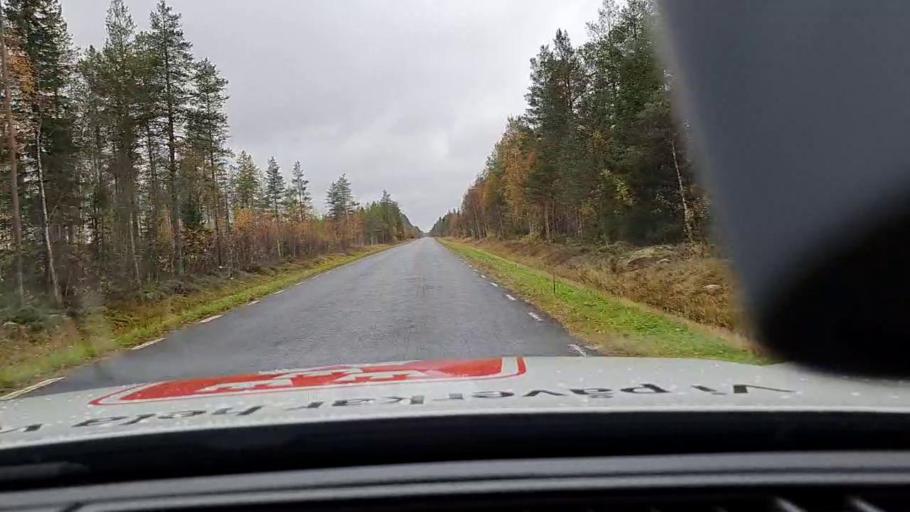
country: SE
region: Norrbotten
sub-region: Haparanda Kommun
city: Haparanda
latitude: 65.9068
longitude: 23.8321
